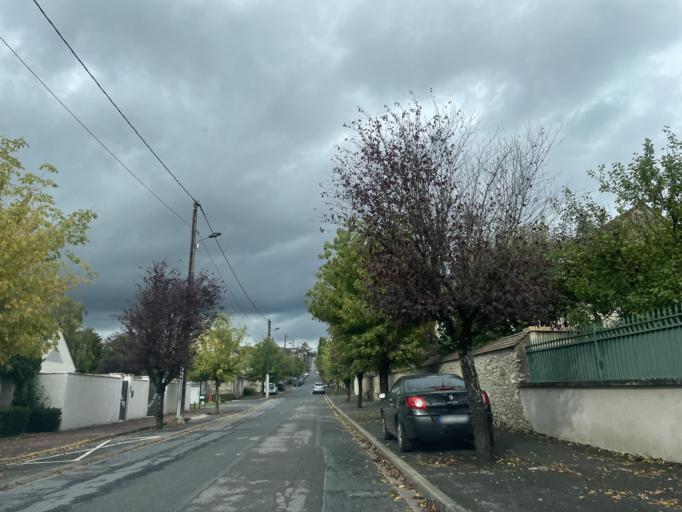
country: FR
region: Ile-de-France
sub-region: Departement de Seine-et-Marne
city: Coulommiers
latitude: 48.8190
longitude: 3.0852
